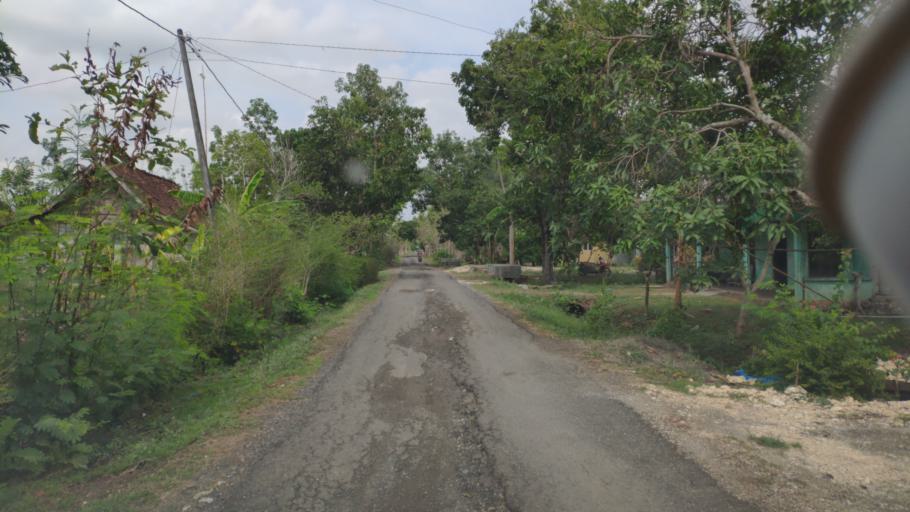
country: ID
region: Central Java
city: Ngablak
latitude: -7.0188
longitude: 111.3858
